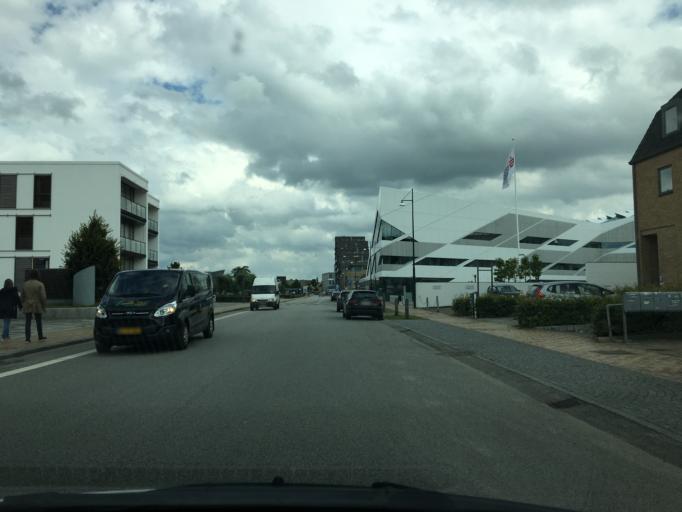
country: DK
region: South Denmark
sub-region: Middelfart Kommune
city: Middelfart
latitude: 55.5059
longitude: 9.7326
